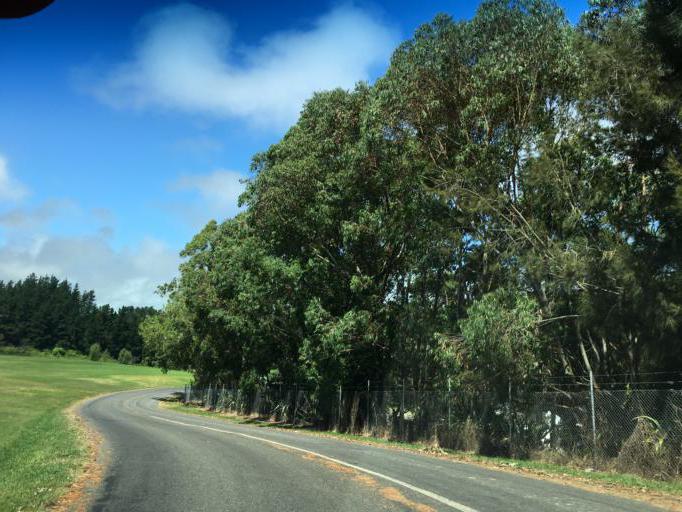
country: NZ
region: Hawke's Bay
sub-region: Wairoa District
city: Wairoa
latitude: -39.0465
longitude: 177.4134
